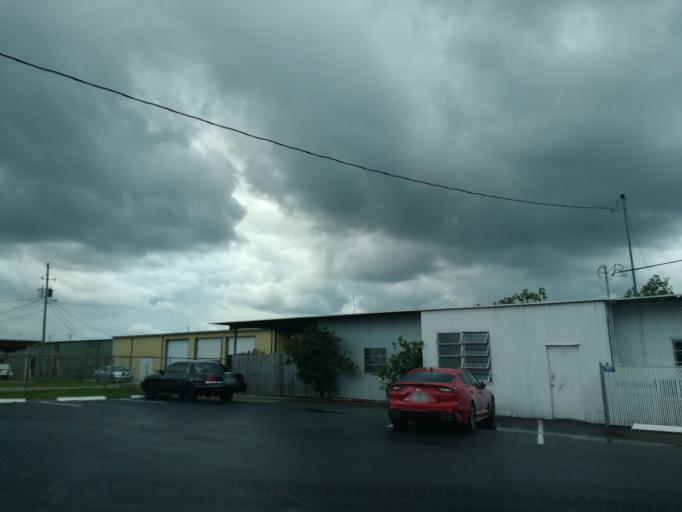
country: US
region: Florida
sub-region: Highlands County
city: Sebring
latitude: 27.4679
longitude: -81.4394
